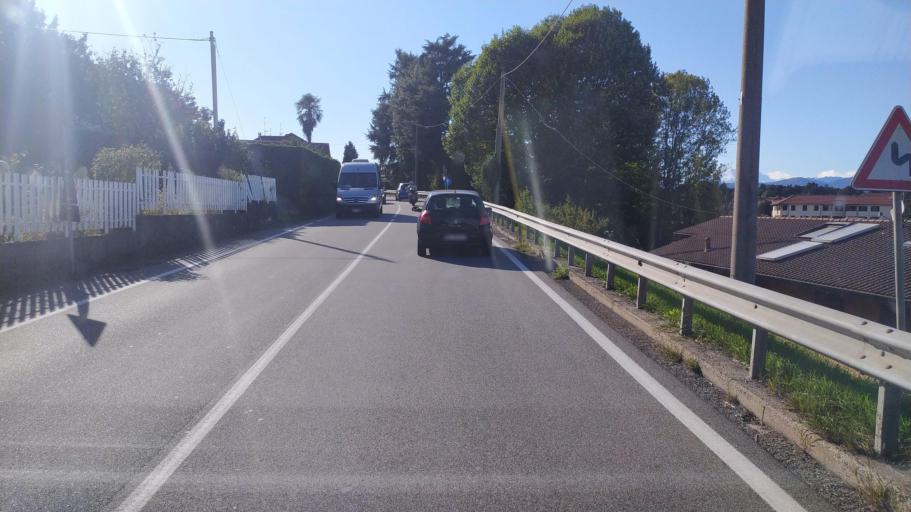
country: IT
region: Lombardy
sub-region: Provincia di Varese
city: Travedona Monate
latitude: 45.8048
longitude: 8.6809
